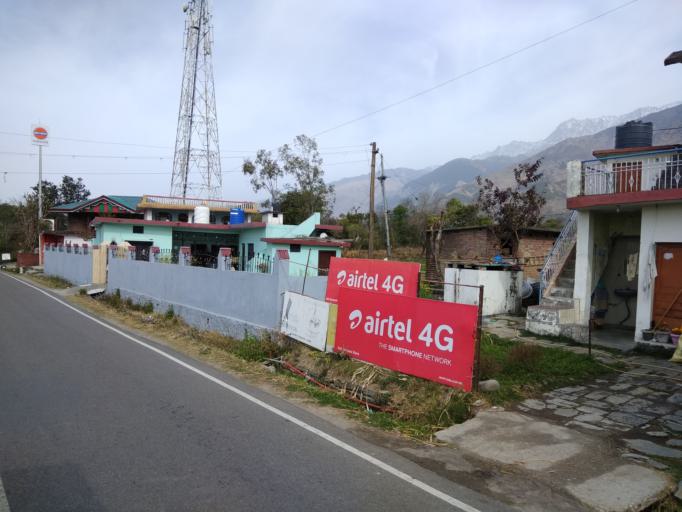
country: IN
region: Himachal Pradesh
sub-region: Kangra
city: Dharmsala
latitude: 32.1645
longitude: 76.3975
